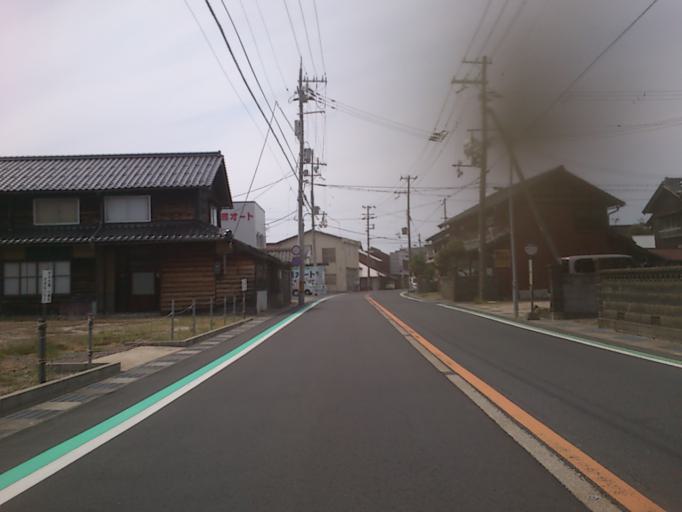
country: JP
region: Kyoto
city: Miyazu
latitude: 35.6836
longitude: 135.0252
